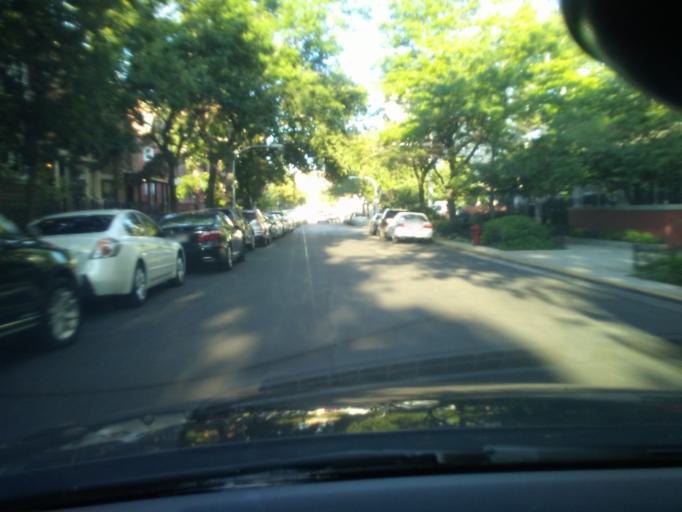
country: US
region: Illinois
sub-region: Cook County
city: Evanston
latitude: 41.9683
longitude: -87.6533
